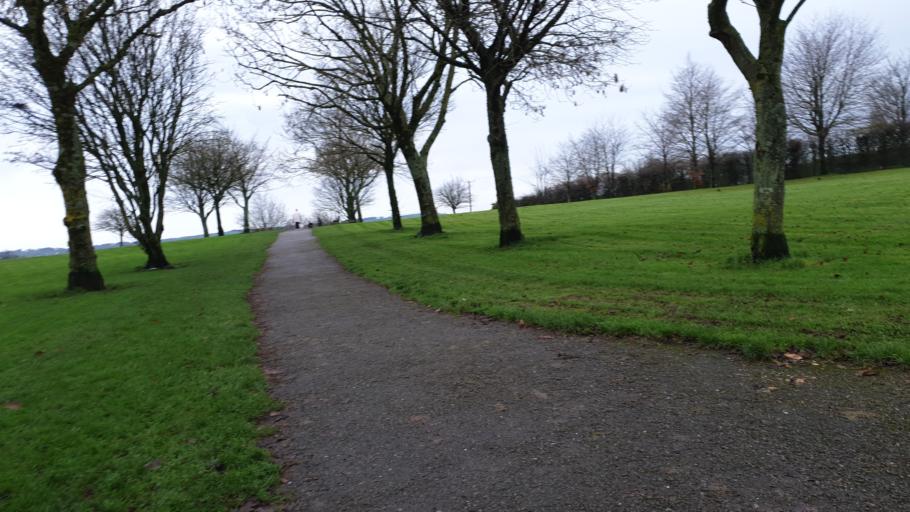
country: IE
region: Munster
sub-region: County Cork
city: Cork
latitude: 51.8898
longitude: -8.4298
